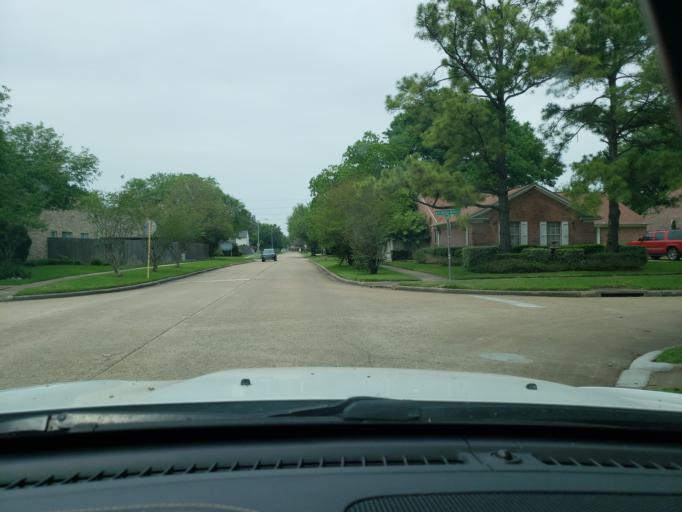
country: US
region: Texas
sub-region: Harris County
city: Jersey Village
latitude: 29.9168
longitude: -95.5740
